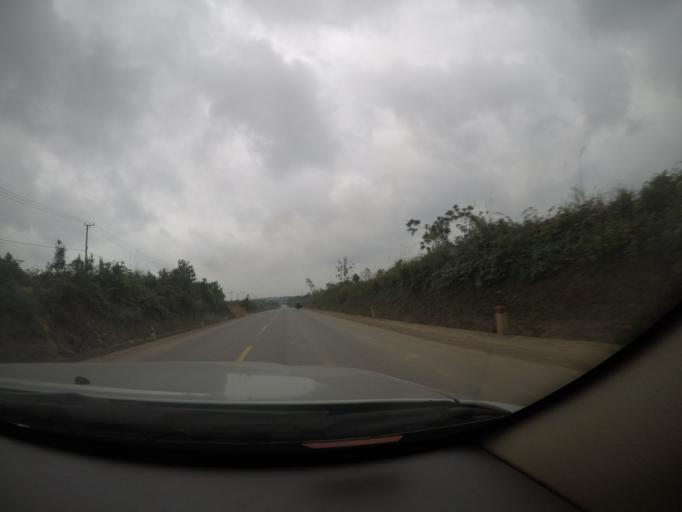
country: VN
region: Quang Tri
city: Dong Ha
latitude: 16.7915
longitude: 107.0546
